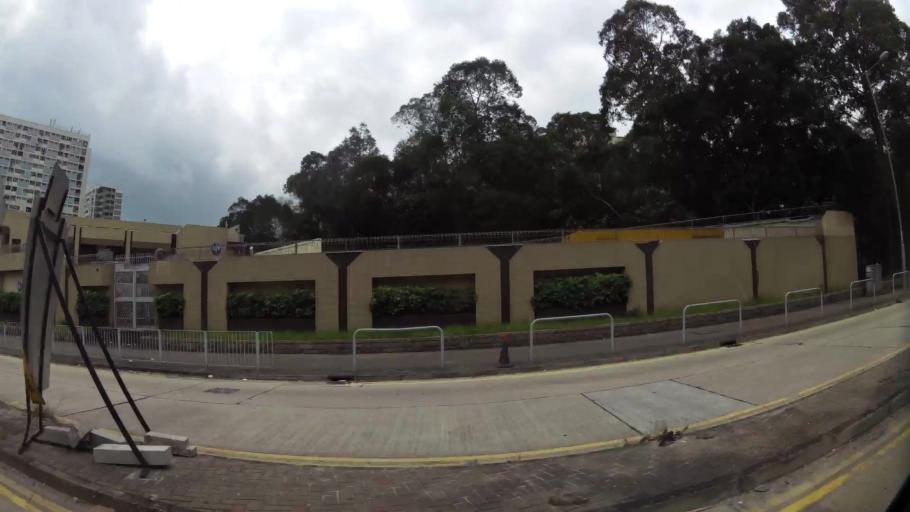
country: HK
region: Wong Tai Sin
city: Wong Tai Sin
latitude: 22.3382
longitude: 114.2042
